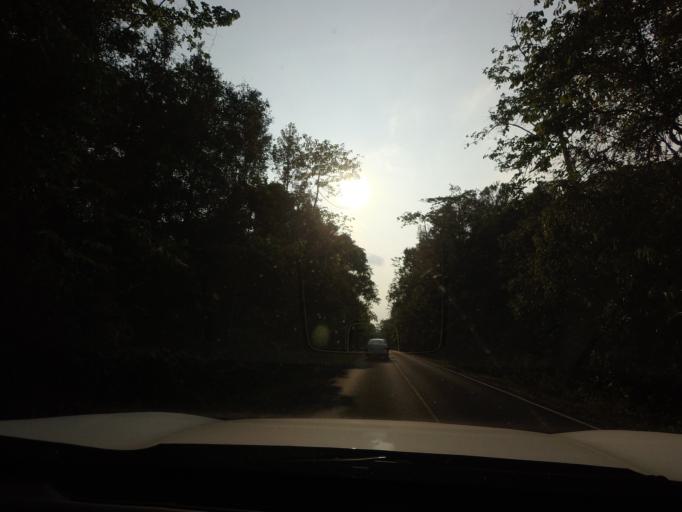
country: TH
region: Nakhon Nayok
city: Nakhon Nayok
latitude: 14.3908
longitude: 101.3580
